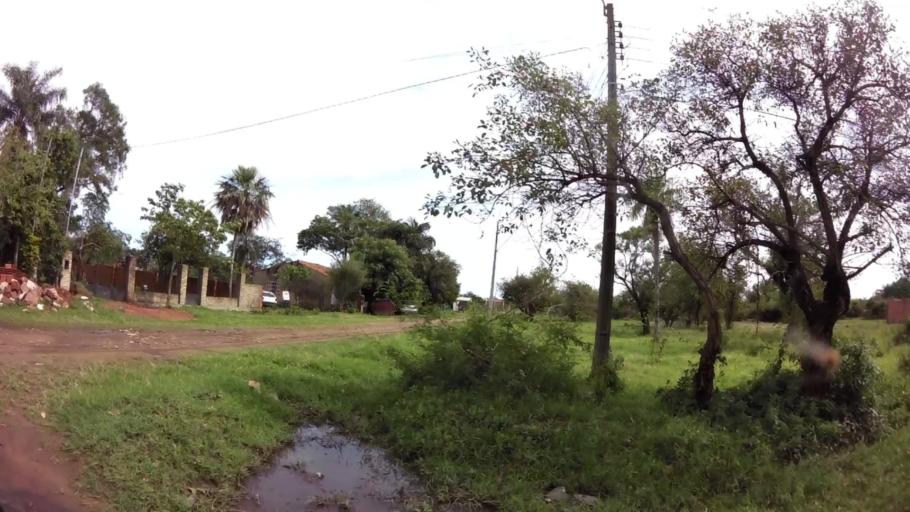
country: PY
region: Central
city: Limpio
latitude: -25.1658
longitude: -57.4842
